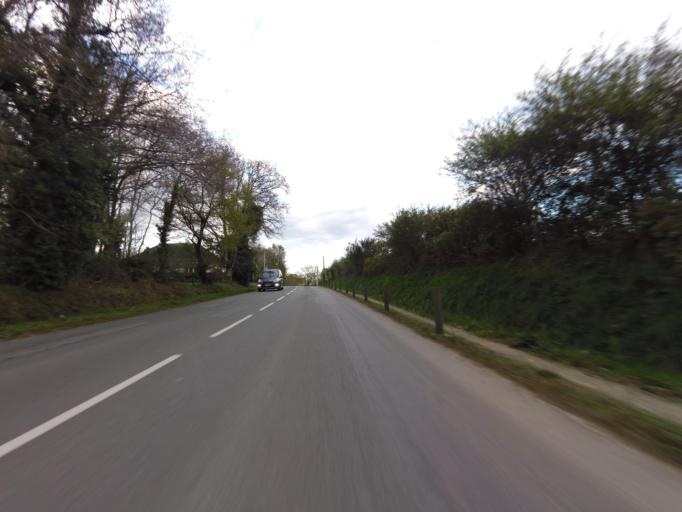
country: FR
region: Brittany
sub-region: Departement du Morbihan
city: Plougoumelen
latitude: 47.6562
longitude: -2.9134
